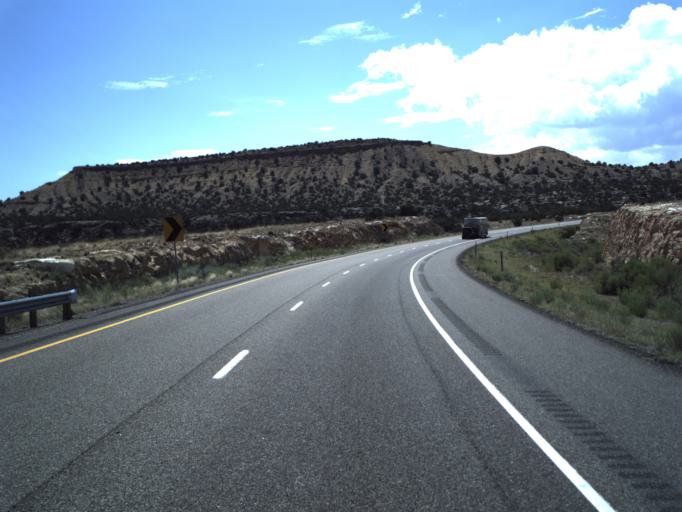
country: US
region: Utah
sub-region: Emery County
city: Castle Dale
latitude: 38.9156
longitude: -110.5031
